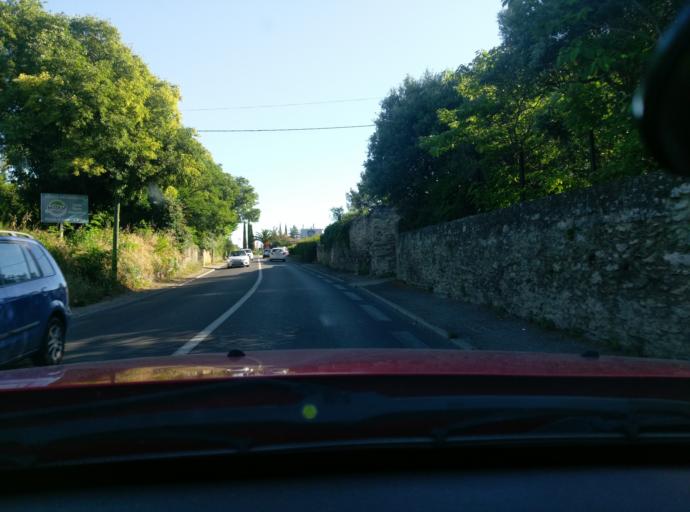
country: FR
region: Languedoc-Roussillon
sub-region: Departement du Gard
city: Uzes
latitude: 44.0018
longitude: 4.4156
